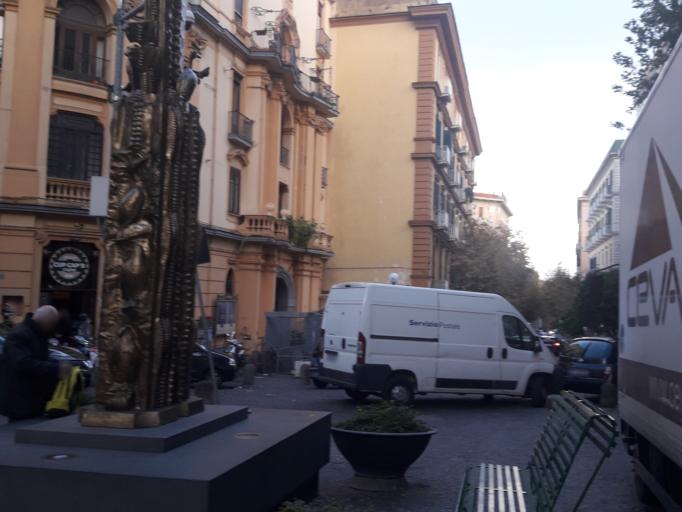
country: IT
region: Campania
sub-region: Provincia di Napoli
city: Napoli
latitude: 40.8428
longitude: 14.2333
